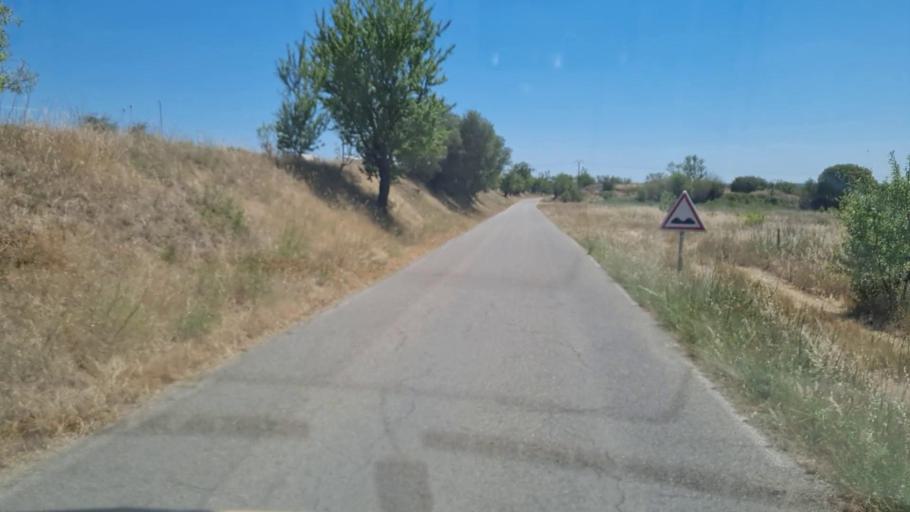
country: FR
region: Languedoc-Roussillon
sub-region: Departement du Gard
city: Vauvert
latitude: 43.6804
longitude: 4.2690
